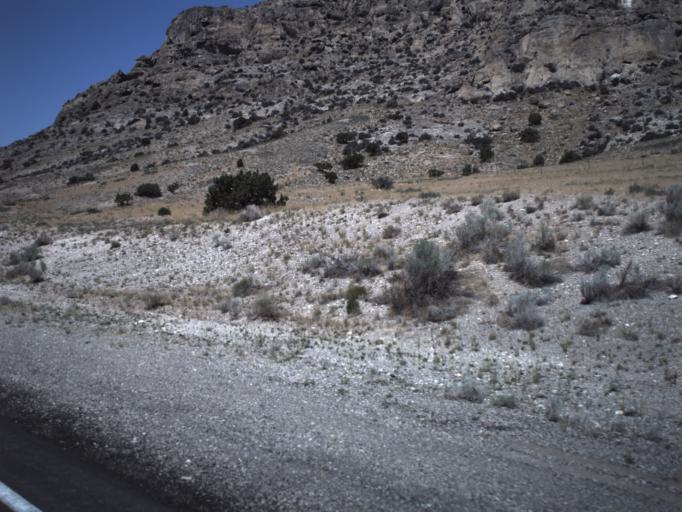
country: US
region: Utah
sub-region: Beaver County
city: Milford
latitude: 39.0721
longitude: -113.6484
